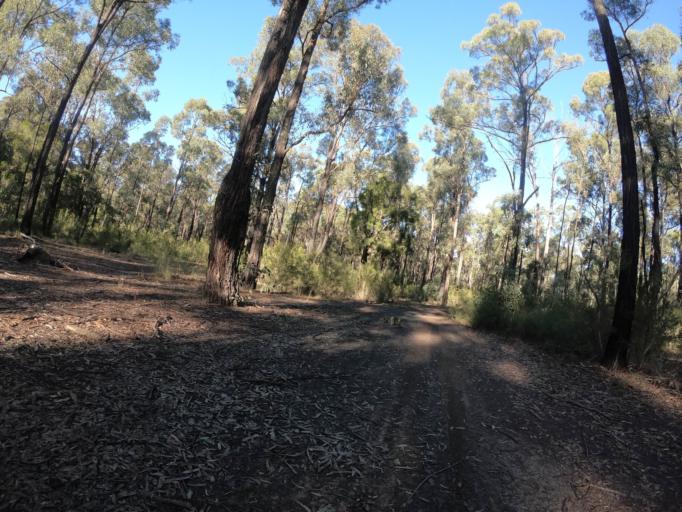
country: AU
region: New South Wales
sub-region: Hawkesbury
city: South Windsor
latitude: -33.6500
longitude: 150.8049
